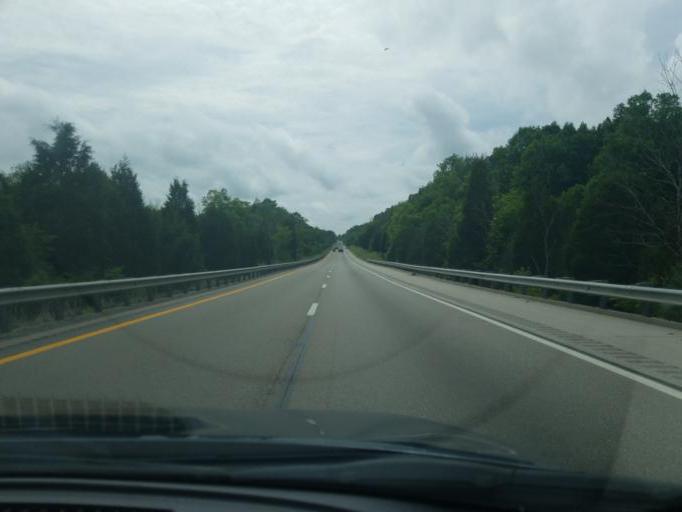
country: US
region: Indiana
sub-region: Switzerland County
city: Vevay
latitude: 38.6776
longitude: -84.9839
